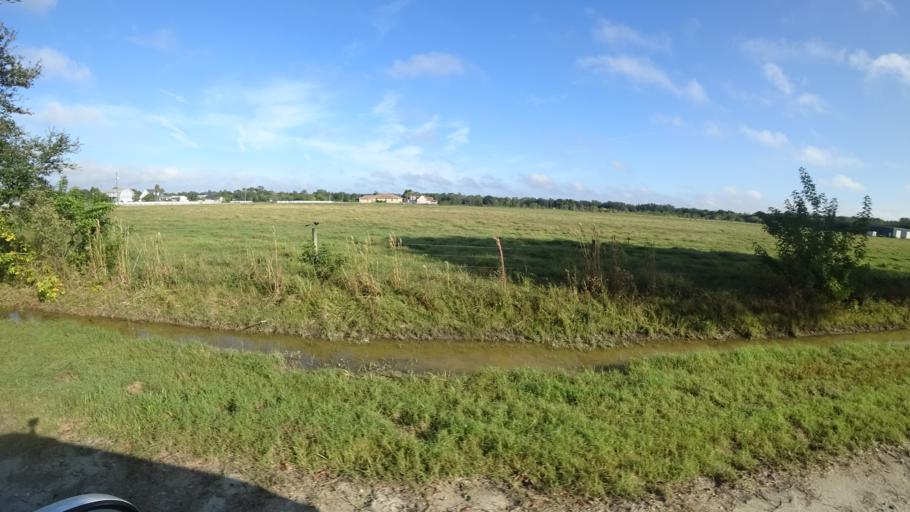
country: US
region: Florida
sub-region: Sarasota County
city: The Meadows
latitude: 27.4311
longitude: -82.3107
